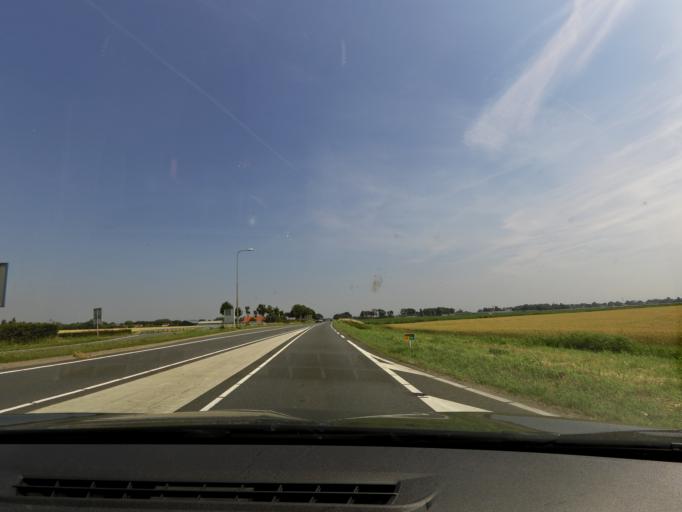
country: NL
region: South Holland
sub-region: Gemeente Binnenmaas
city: Heinenoord
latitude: 51.8234
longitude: 4.4468
